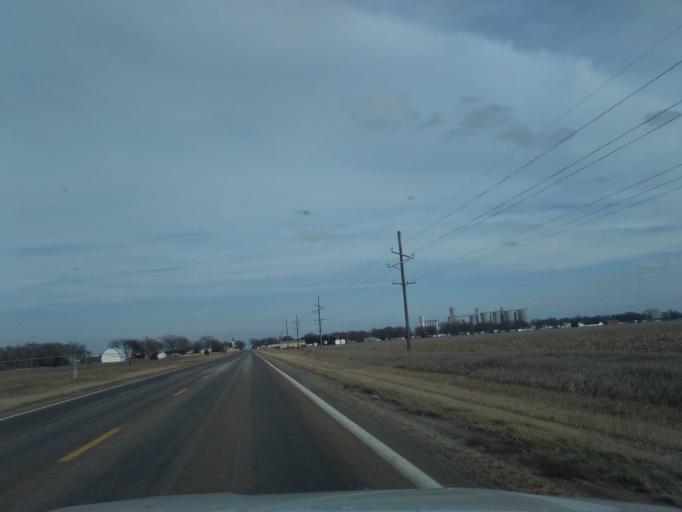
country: US
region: Nebraska
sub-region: Saline County
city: Wilber
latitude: 40.3061
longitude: -97.0034
